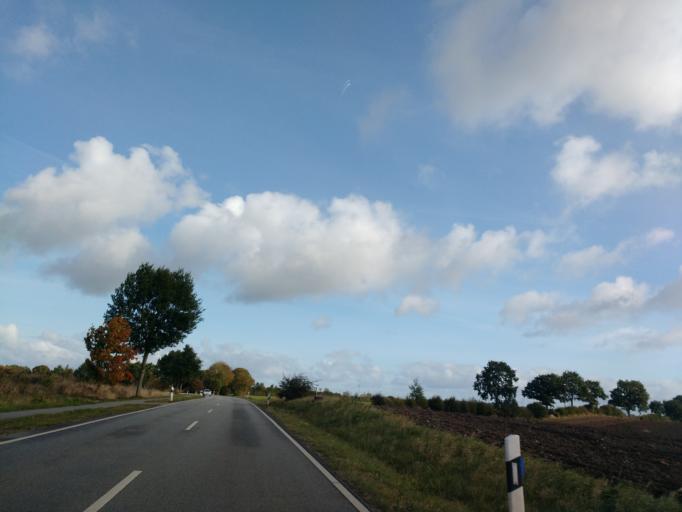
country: DE
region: Schleswig-Holstein
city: Neustadt in Holstein
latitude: 54.1217
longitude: 10.8208
